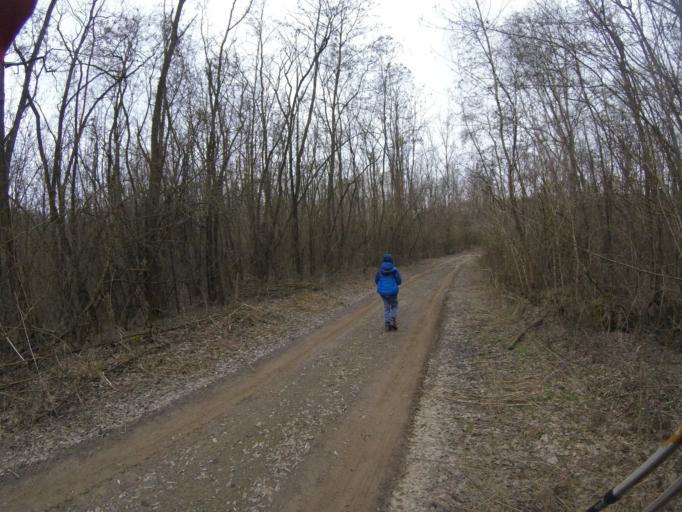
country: HU
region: Borsod-Abauj-Zemplen
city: Rudabanya
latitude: 48.3977
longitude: 20.6464
